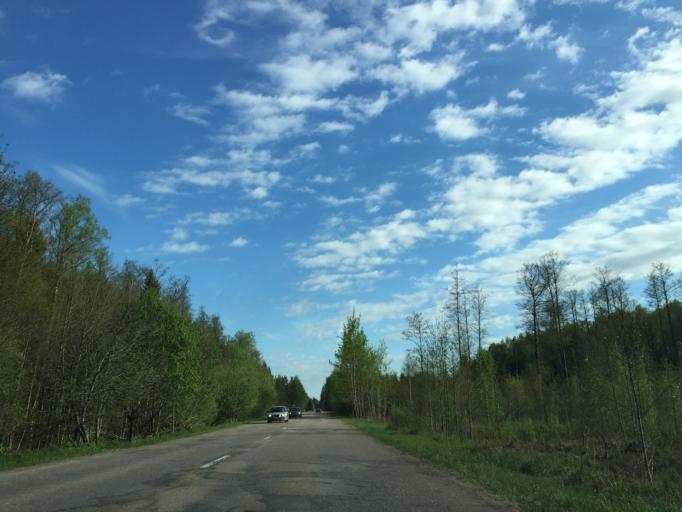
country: LV
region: Lecava
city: Iecava
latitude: 56.7097
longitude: 24.1128
